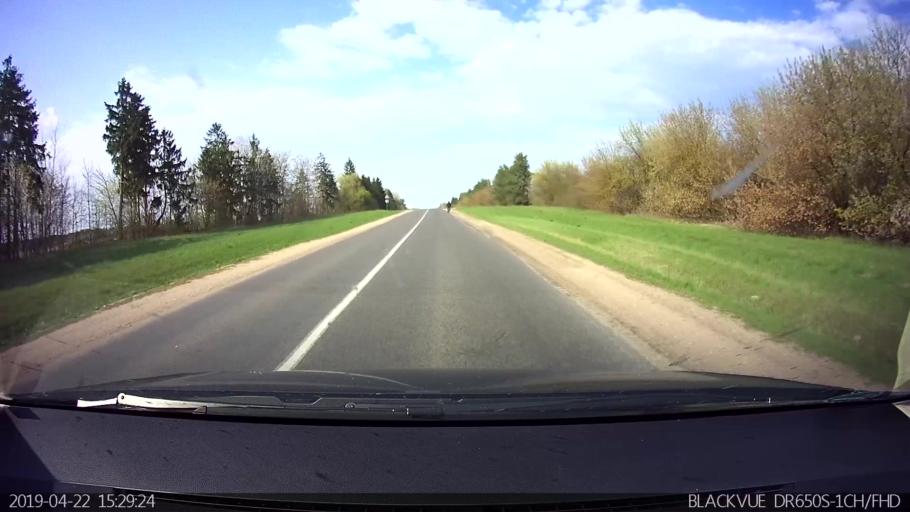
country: BY
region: Brest
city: Vysokaye
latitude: 52.3856
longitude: 23.3734
